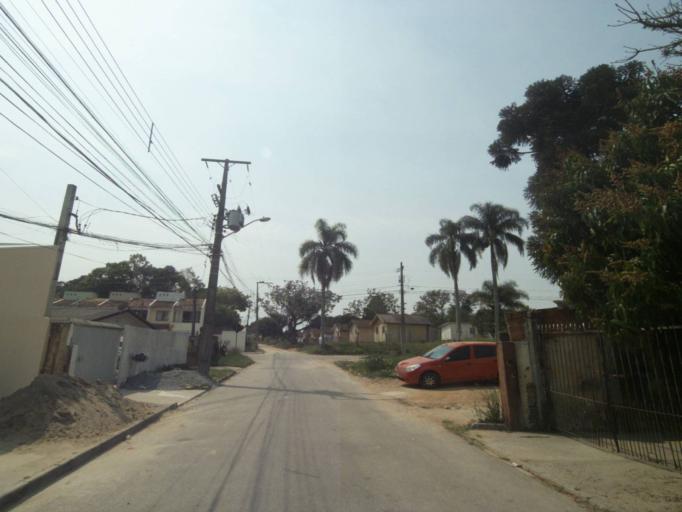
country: BR
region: Parana
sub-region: Pinhais
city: Pinhais
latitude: -25.4836
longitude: -49.2159
